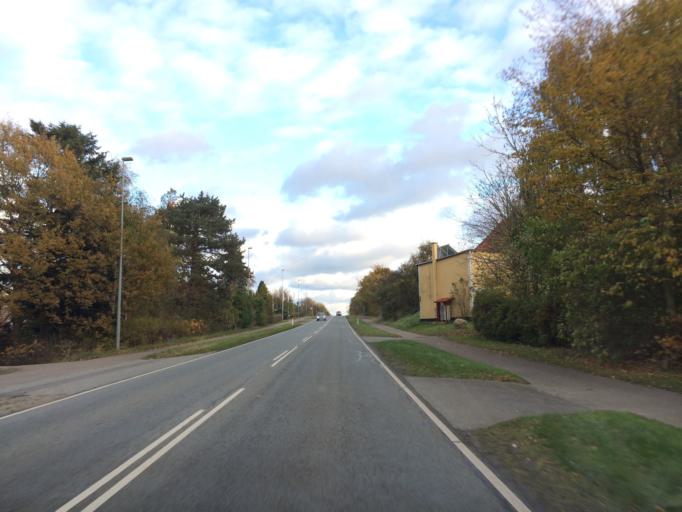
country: DK
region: South Denmark
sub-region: Sonderborg Kommune
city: Nordborg
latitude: 55.0418
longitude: 9.7970
